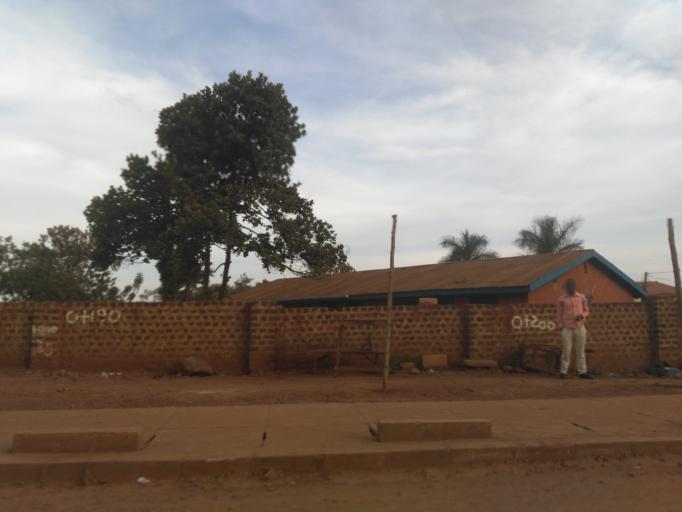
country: UG
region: Eastern Region
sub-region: Jinja District
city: Jinja
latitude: 0.4341
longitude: 33.2123
